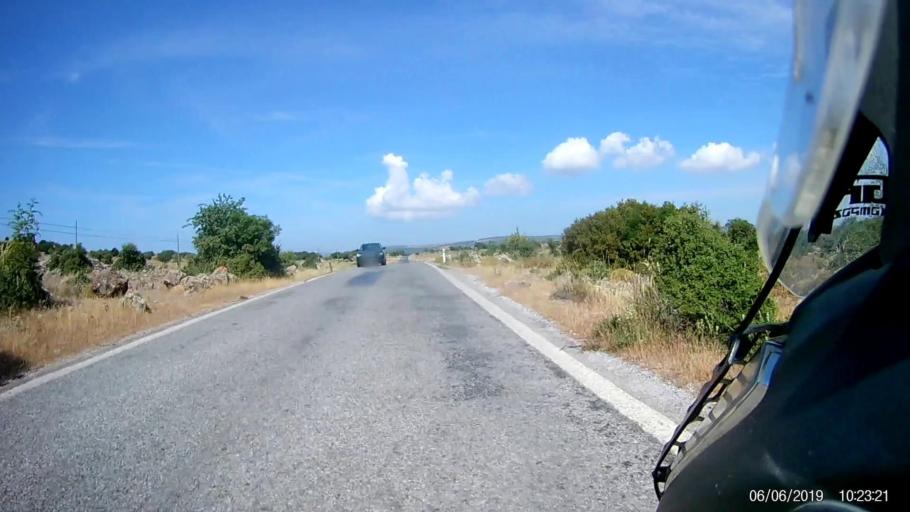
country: TR
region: Canakkale
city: Behram
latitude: 39.5082
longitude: 26.4228
